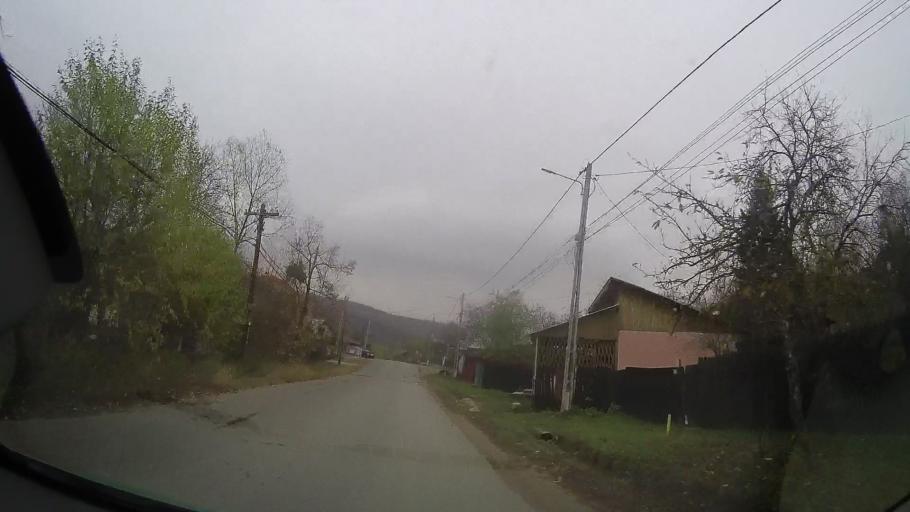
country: RO
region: Prahova
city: Ceptura de Sus
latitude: 45.0365
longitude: 26.3133
